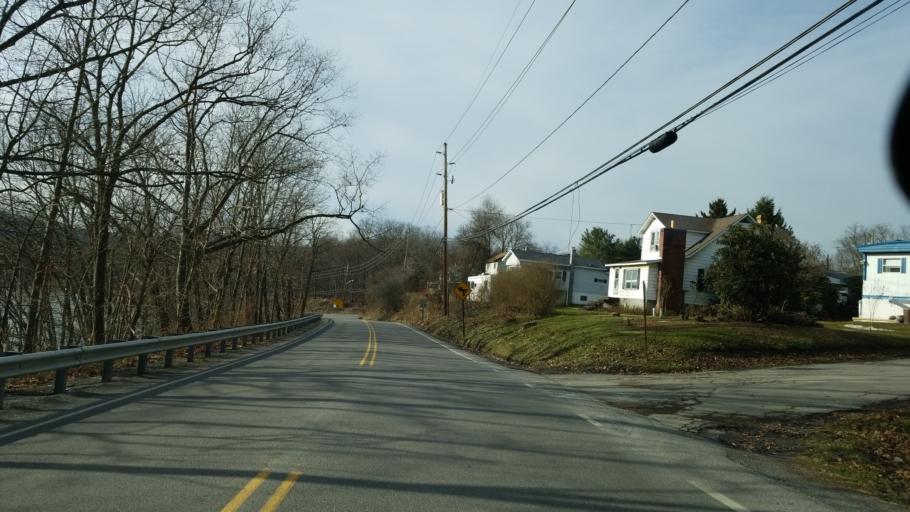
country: US
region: Pennsylvania
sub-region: Clearfield County
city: Clearfield
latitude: 41.0338
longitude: -78.4292
